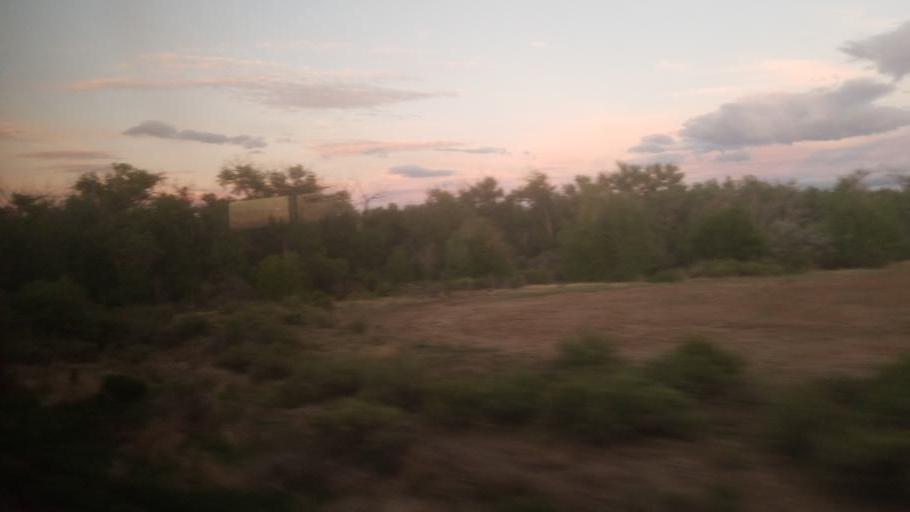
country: US
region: Colorado
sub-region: Las Animas County
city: Trinidad
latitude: 37.2404
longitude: -104.4272
